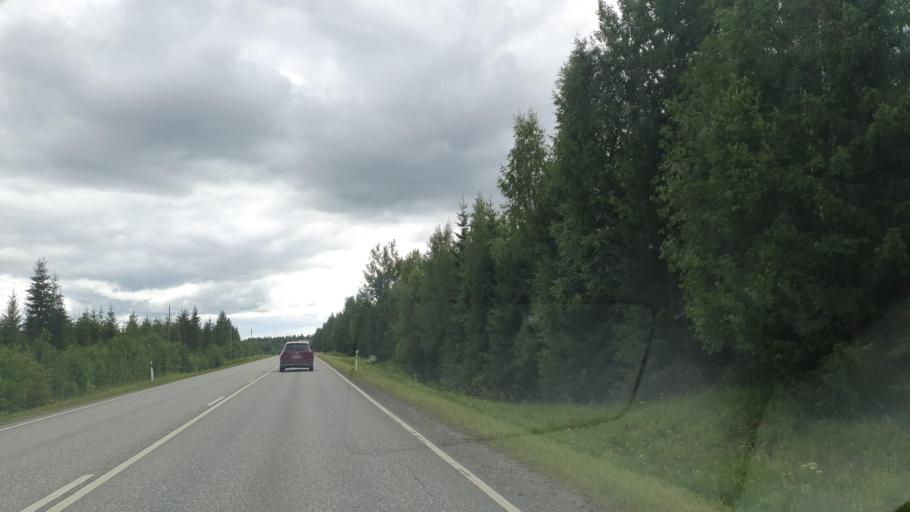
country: FI
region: Northern Savo
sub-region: Ylae-Savo
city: Sonkajaervi
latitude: 63.7147
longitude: 27.3627
